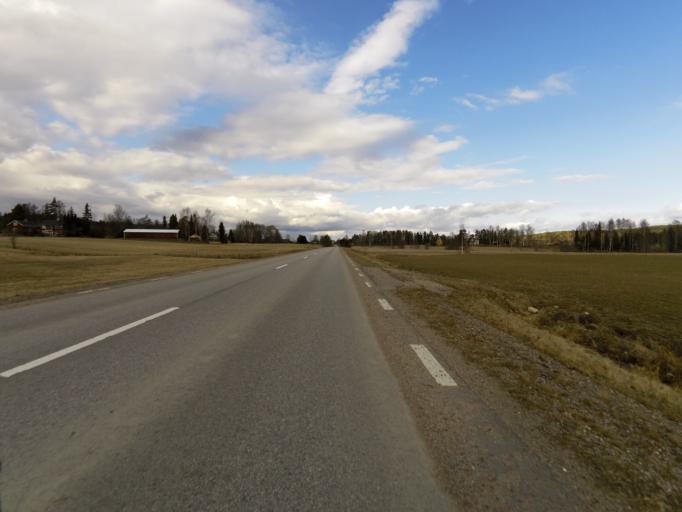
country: SE
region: Dalarna
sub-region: Avesta Kommun
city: Horndal
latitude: 60.4554
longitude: 16.4540
